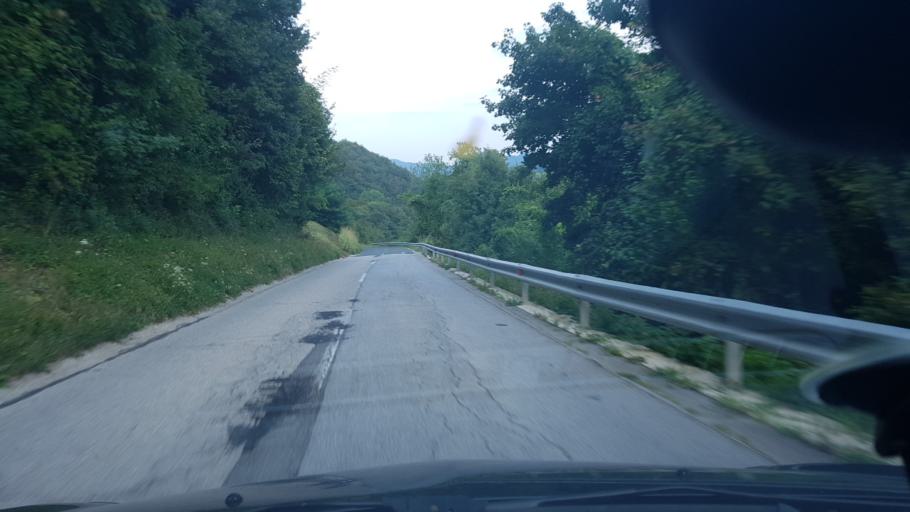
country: SI
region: Kozje
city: Kozje
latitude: 46.0414
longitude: 15.5785
